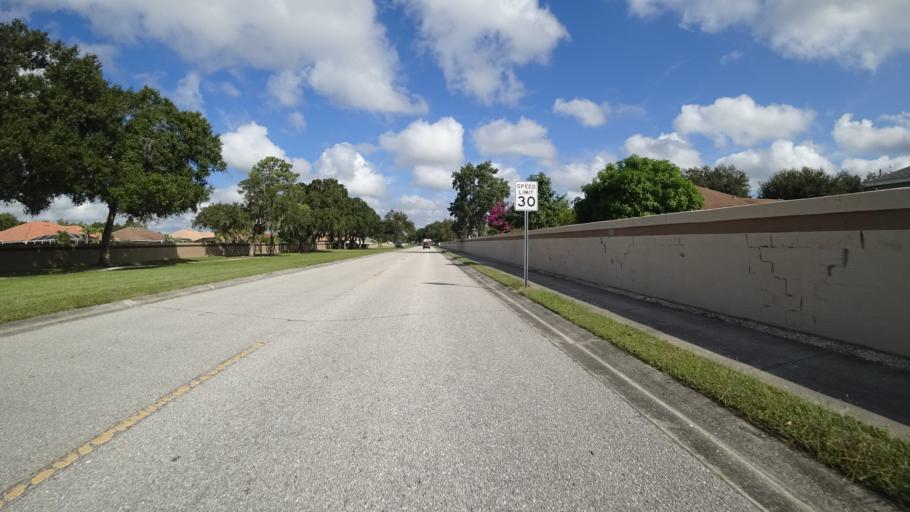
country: US
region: Florida
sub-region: Sarasota County
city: North Sarasota
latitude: 27.4082
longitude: -82.5134
